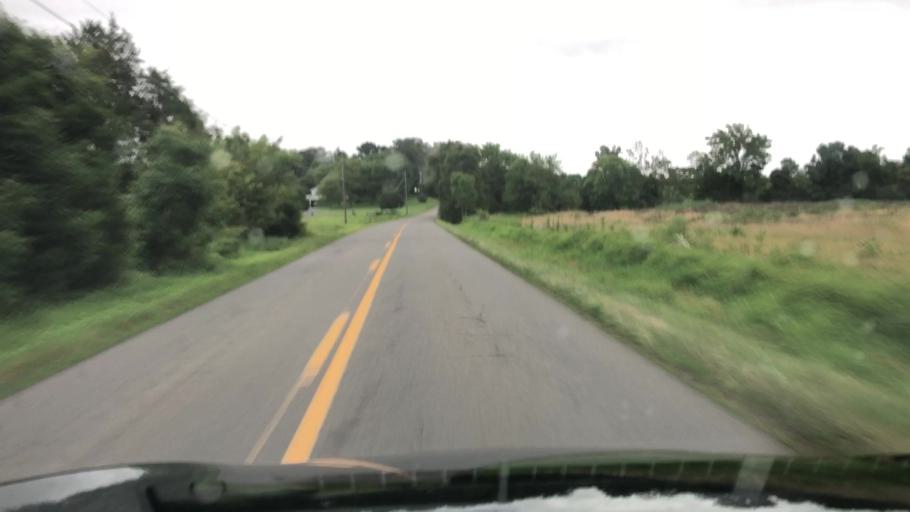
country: US
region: Virginia
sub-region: Prince William County
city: Nokesville
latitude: 38.6756
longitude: -77.6595
